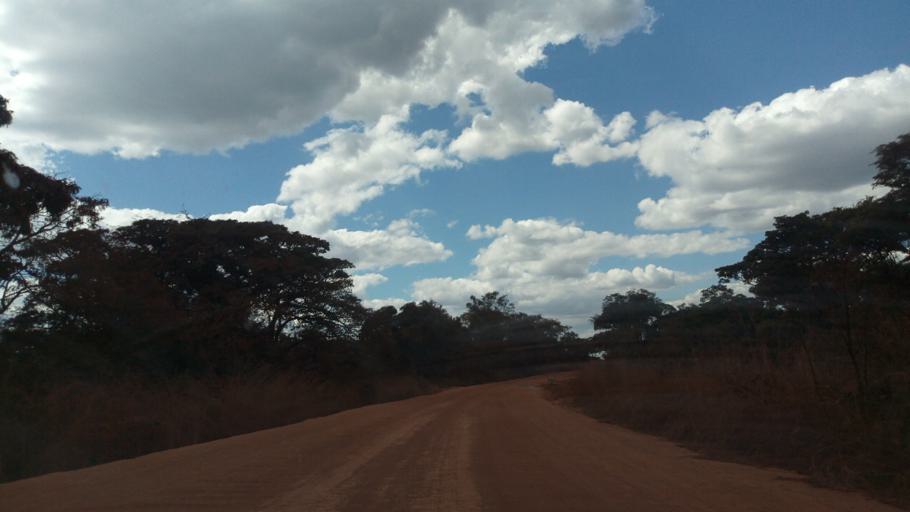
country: ZM
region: Copperbelt
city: Mufulira
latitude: -12.0299
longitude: 28.6731
